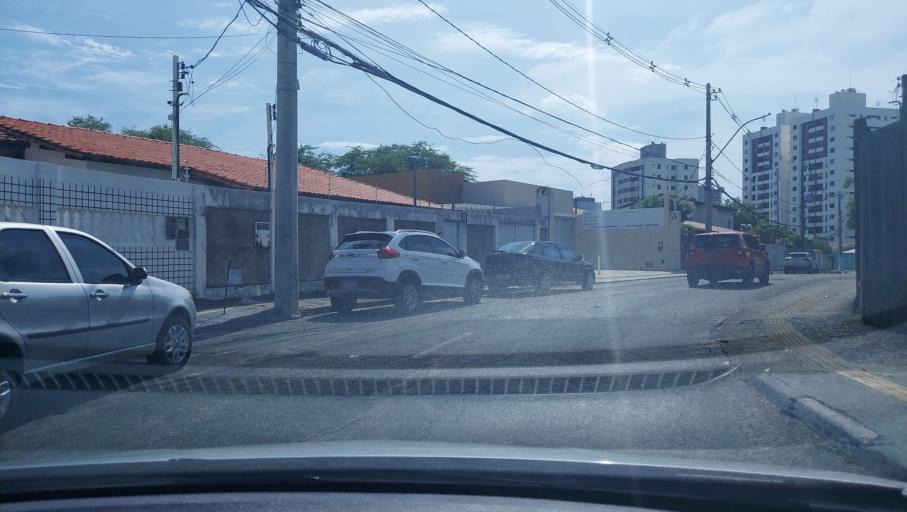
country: BR
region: Bahia
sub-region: Salvador
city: Salvador
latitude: -12.9827
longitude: -38.4466
